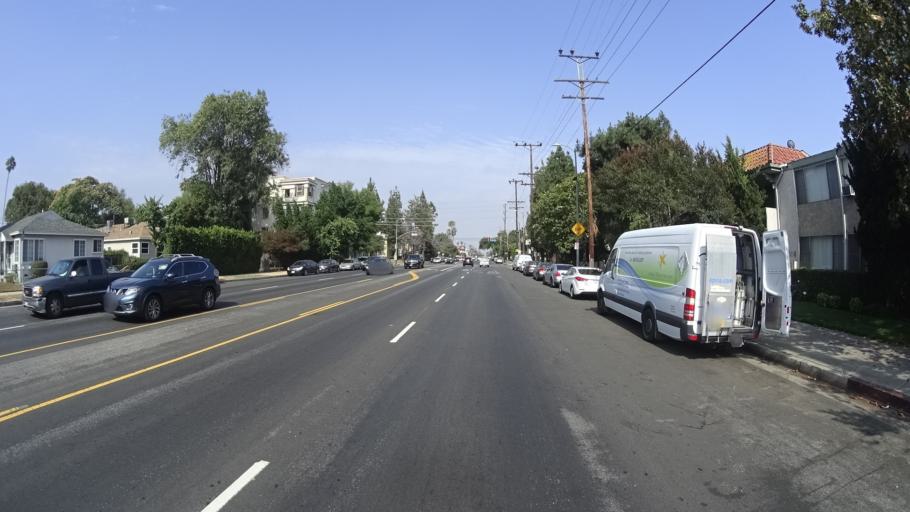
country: US
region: California
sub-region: Los Angeles County
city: Van Nuys
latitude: 34.1721
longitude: -118.4454
